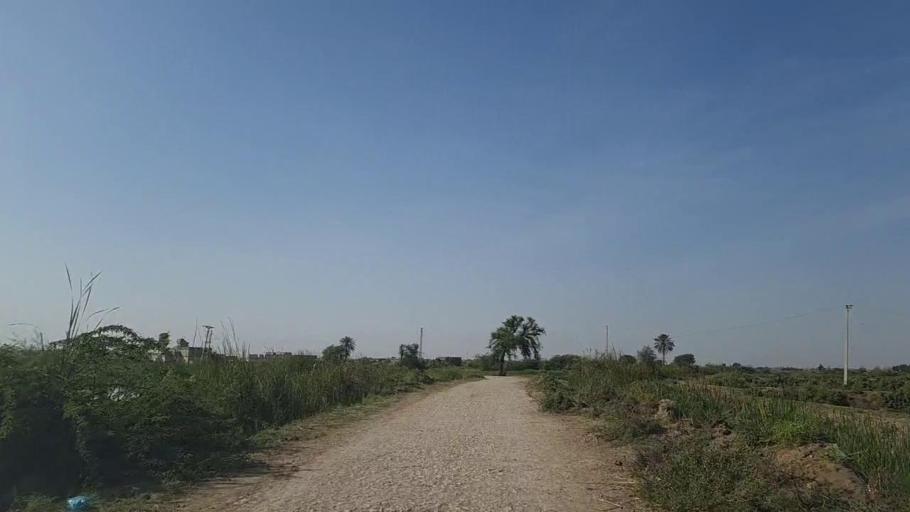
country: PK
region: Sindh
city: Thatta
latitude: 24.5919
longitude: 67.8884
